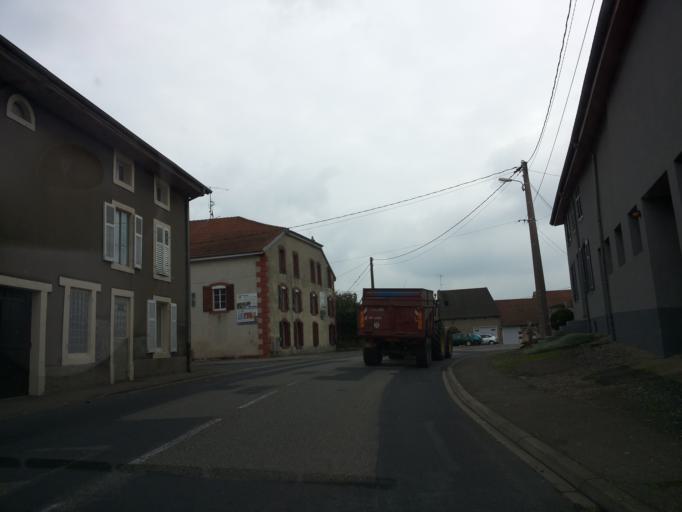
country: FR
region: Lorraine
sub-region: Departement de la Moselle
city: Vic-sur-Seille
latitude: 48.7523
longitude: 6.6284
